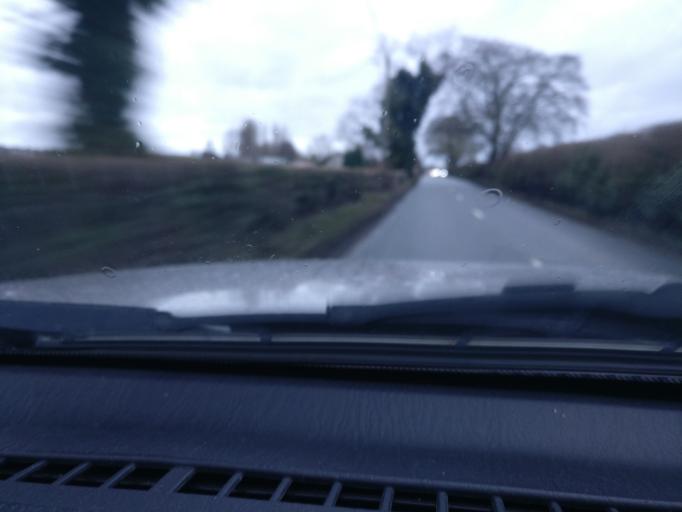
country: IE
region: Leinster
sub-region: An Mhi
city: Trim
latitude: 53.5135
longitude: -6.8391
